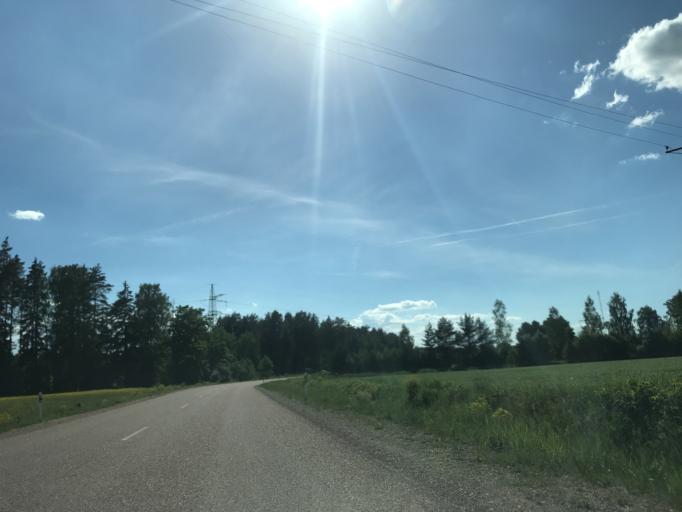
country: LV
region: Koknese
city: Koknese
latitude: 56.5659
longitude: 25.5115
